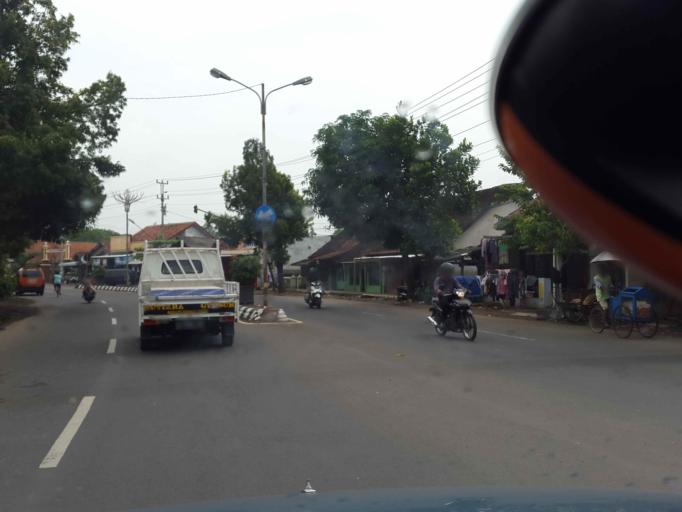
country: ID
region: Central Java
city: Kedungwuni
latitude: -6.9611
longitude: 109.6384
